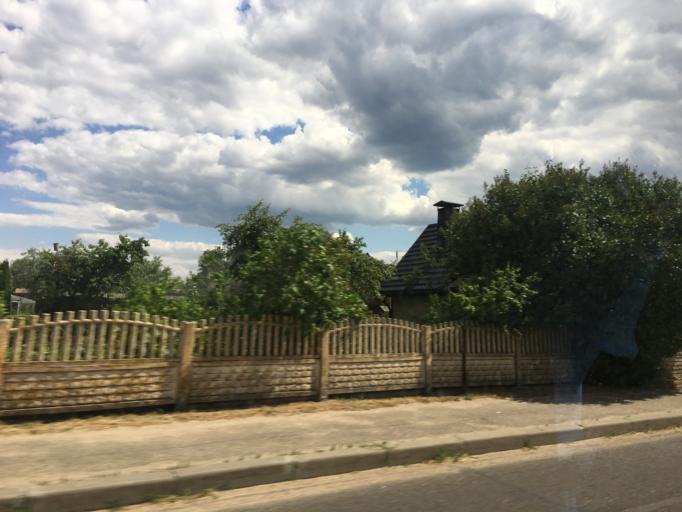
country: LT
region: Alytaus apskritis
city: Druskininkai
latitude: 53.8887
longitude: 24.1384
